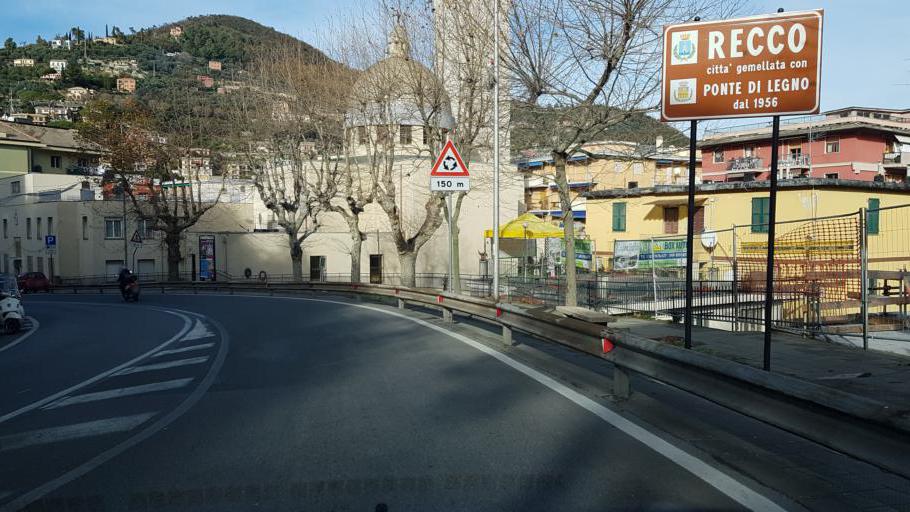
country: IT
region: Liguria
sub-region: Provincia di Genova
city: Recco
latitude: 44.3606
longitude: 9.1452
